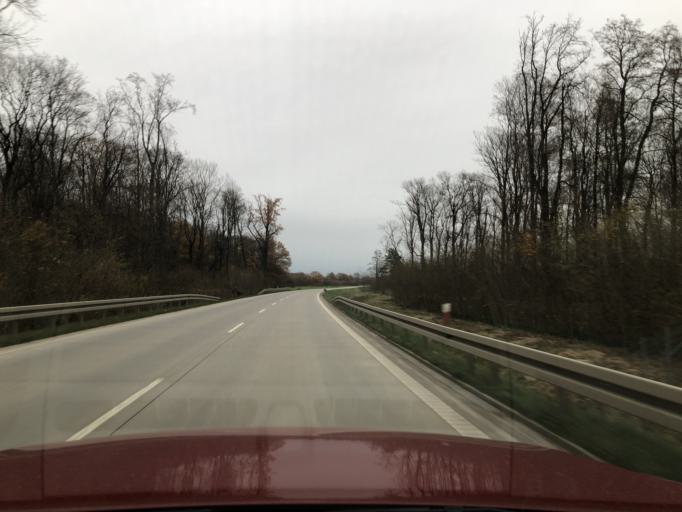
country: PL
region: Lower Silesian Voivodeship
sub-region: Powiat swidnicki
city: Zarow
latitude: 50.9453
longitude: 16.4773
